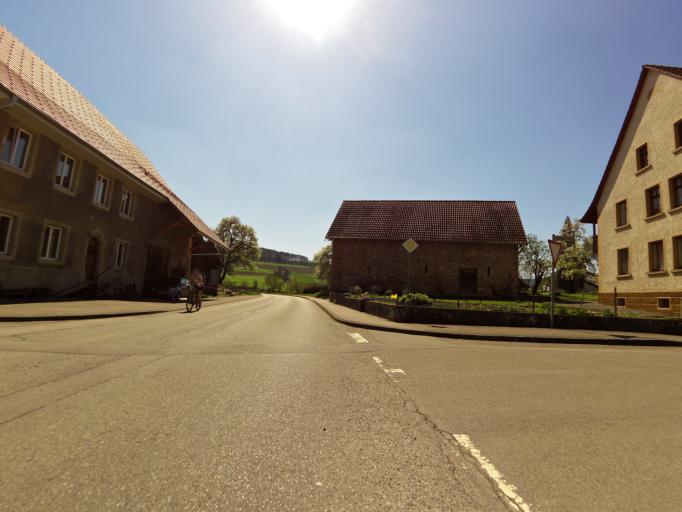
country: DE
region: Baden-Wuerttemberg
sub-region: Freiburg Region
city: Hohentengen am Hochrhein
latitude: 47.5719
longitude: 8.3741
